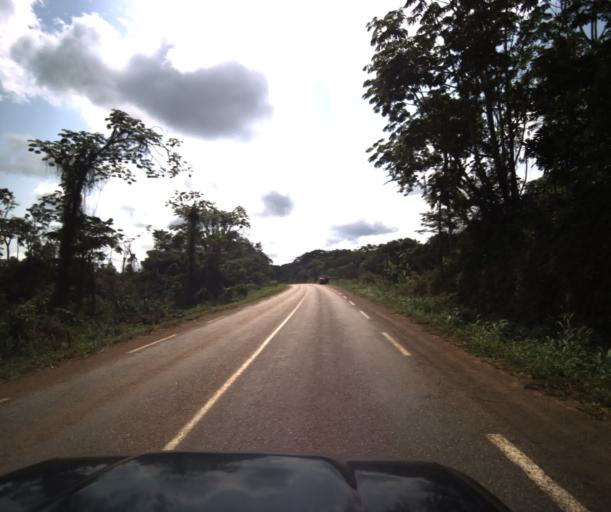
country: CM
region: Centre
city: Eseka
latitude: 3.8716
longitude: 10.6329
